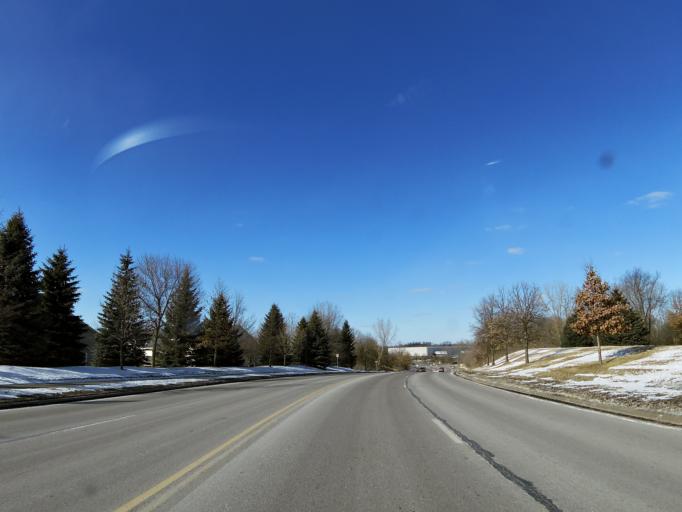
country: US
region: Minnesota
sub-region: Washington County
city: Woodbury
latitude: 44.9090
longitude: -92.9749
